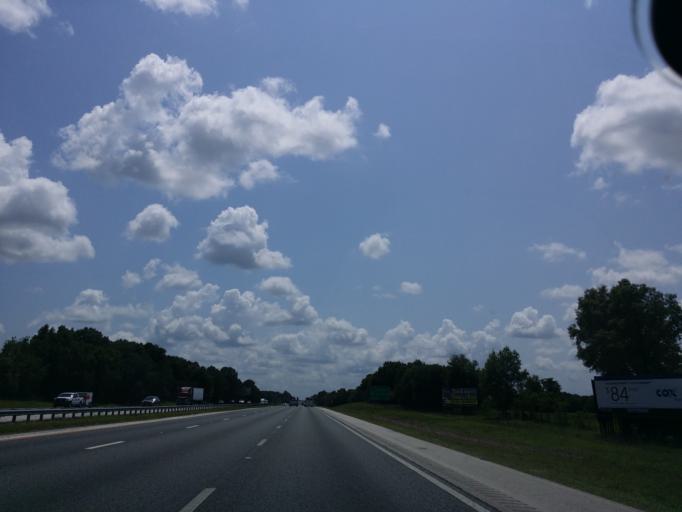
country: US
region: Florida
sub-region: Marion County
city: Ocala
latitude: 29.1344
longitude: -82.1849
